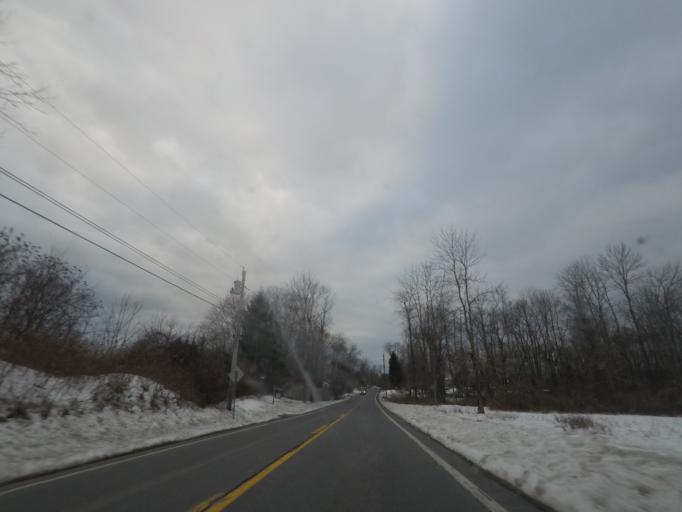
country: US
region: New York
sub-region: Ulster County
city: Clintondale
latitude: 41.6926
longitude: -74.1029
